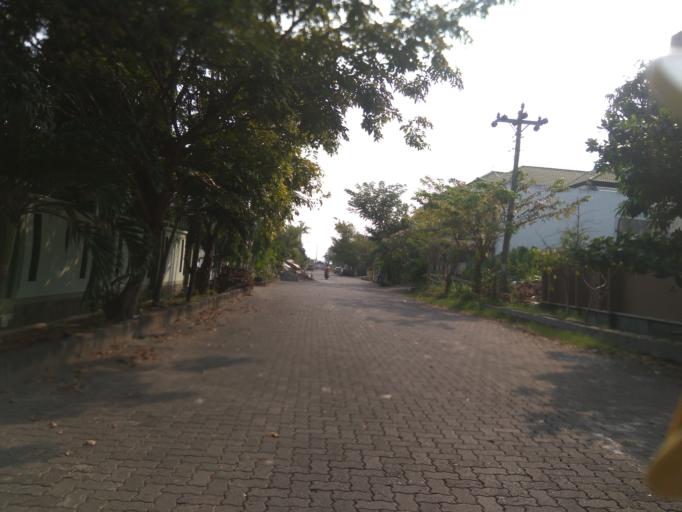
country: ID
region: Central Java
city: Semarang
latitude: -6.9656
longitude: 110.3861
